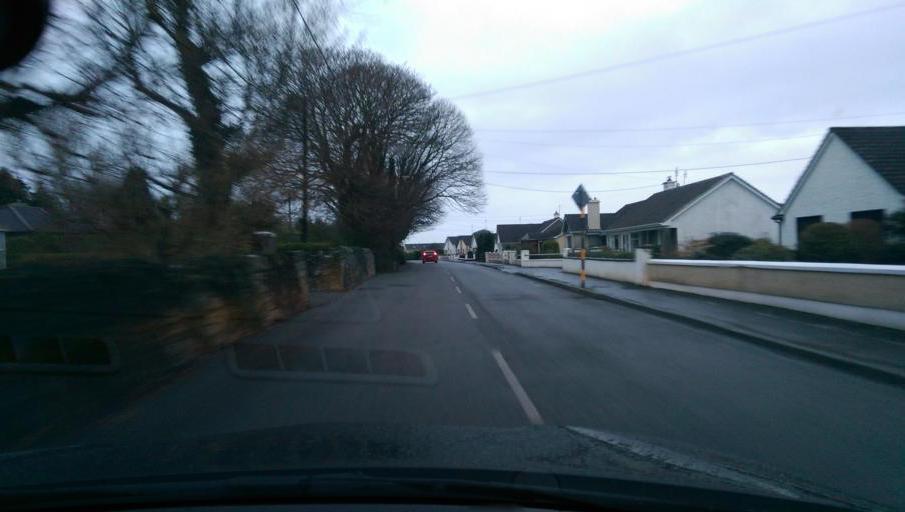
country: IE
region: Connaught
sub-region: County Galway
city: Athenry
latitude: 53.3033
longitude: -8.7474
